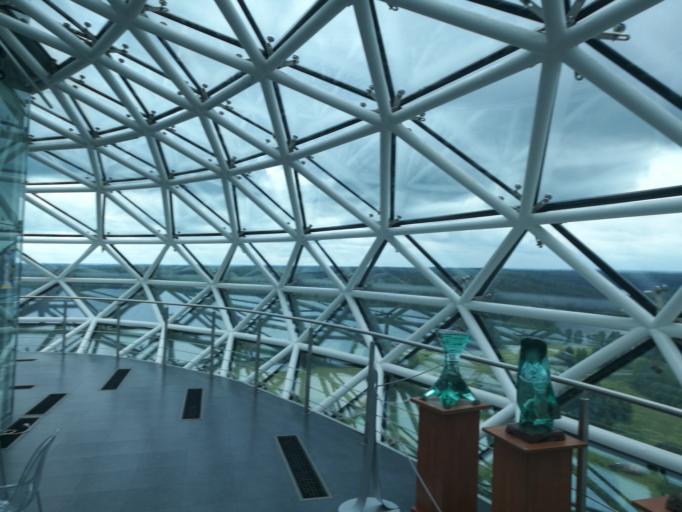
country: LT
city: Moletai
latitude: 55.3154
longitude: 25.5548
